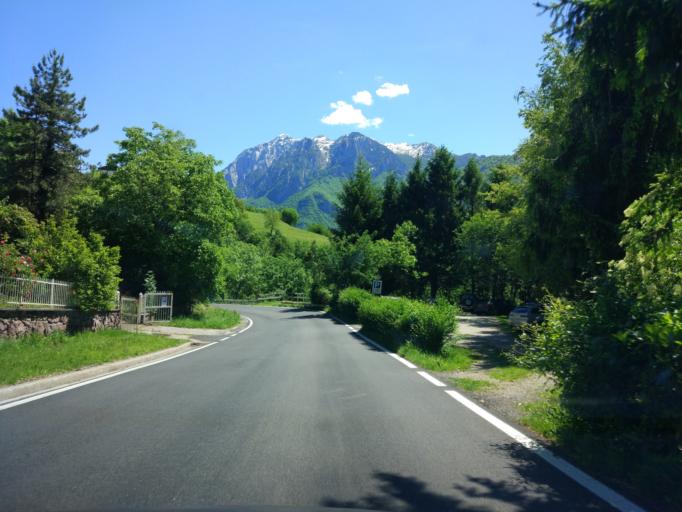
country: IT
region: Lombardy
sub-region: Provincia di Lecco
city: Crandola Valsassina
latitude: 46.0245
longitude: 9.3728
